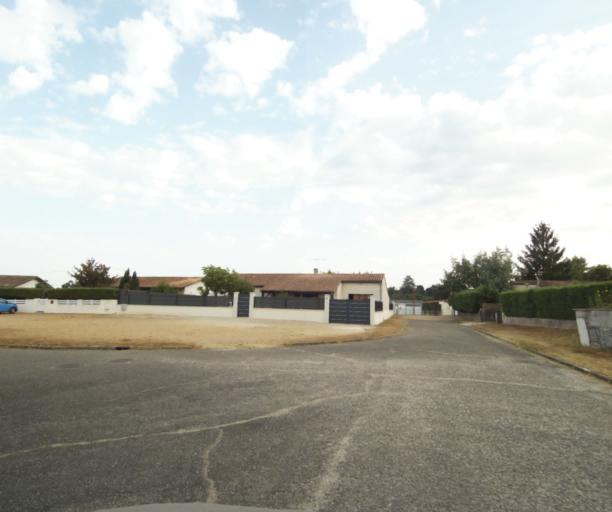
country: FR
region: Aquitaine
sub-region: Departement de la Gironde
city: Creon
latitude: 44.7739
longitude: -0.3546
